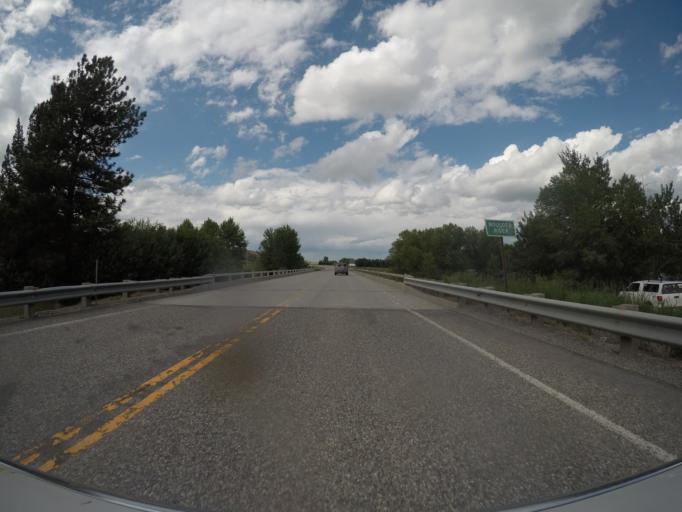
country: US
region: Montana
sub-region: Sweet Grass County
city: Big Timber
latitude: 45.7229
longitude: -109.9968
